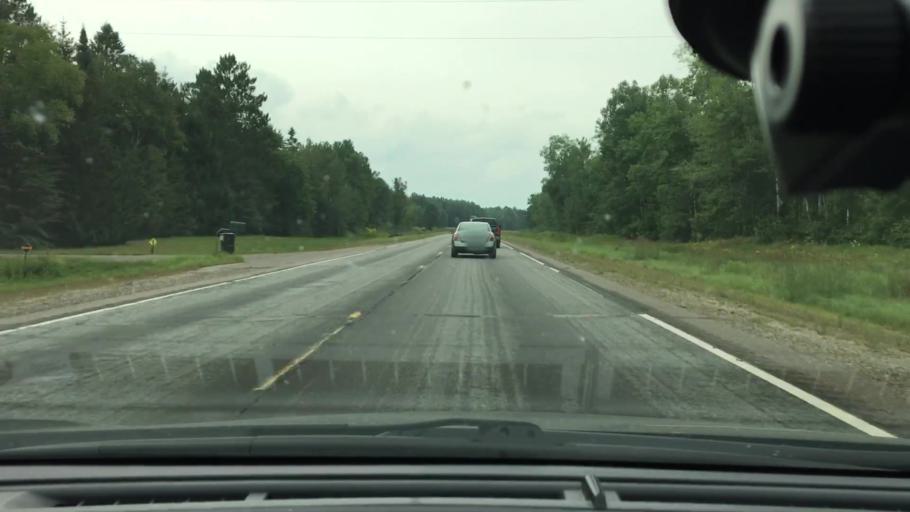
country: US
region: Minnesota
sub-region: Crow Wing County
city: Cross Lake
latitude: 46.6748
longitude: -93.9522
